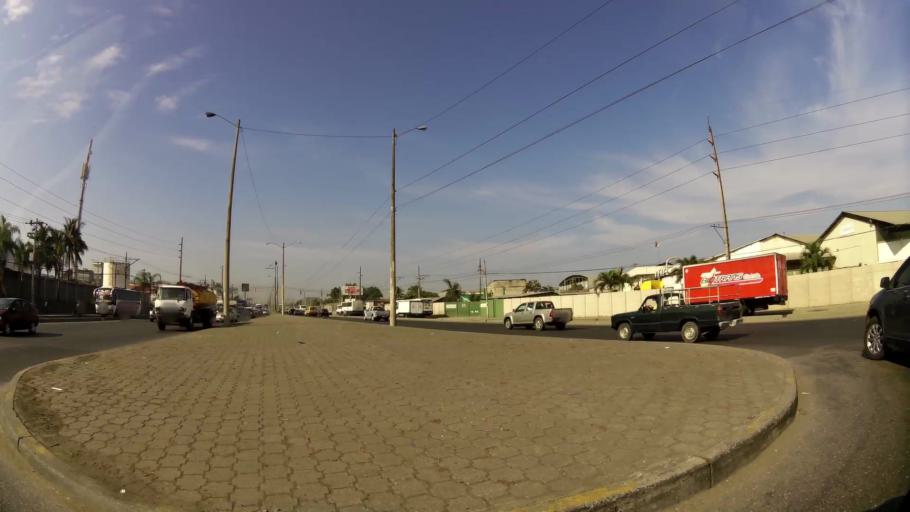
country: EC
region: Guayas
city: Santa Lucia
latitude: -2.0691
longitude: -79.9423
